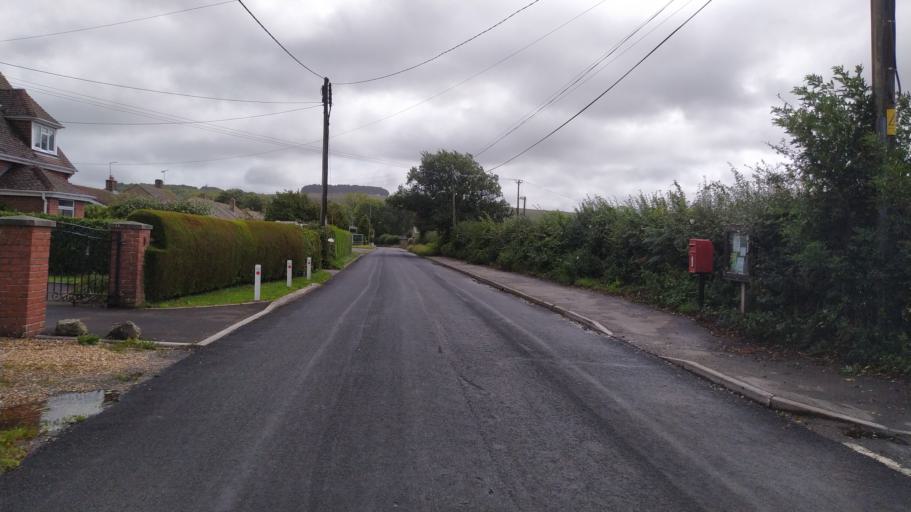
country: GB
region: England
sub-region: Dorset
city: Shaftesbury
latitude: 50.9878
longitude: -2.1682
